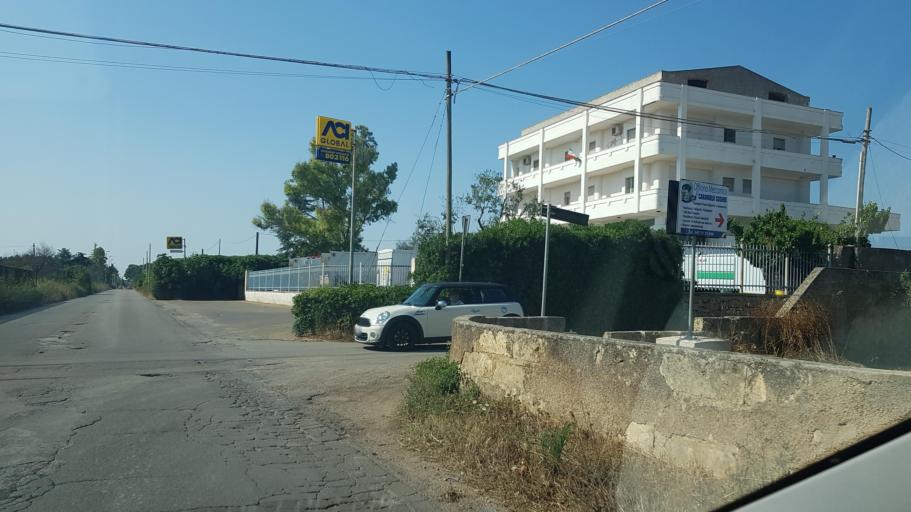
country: IT
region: Apulia
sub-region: Provincia di Lecce
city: Taurisano
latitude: 39.9432
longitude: 18.2233
